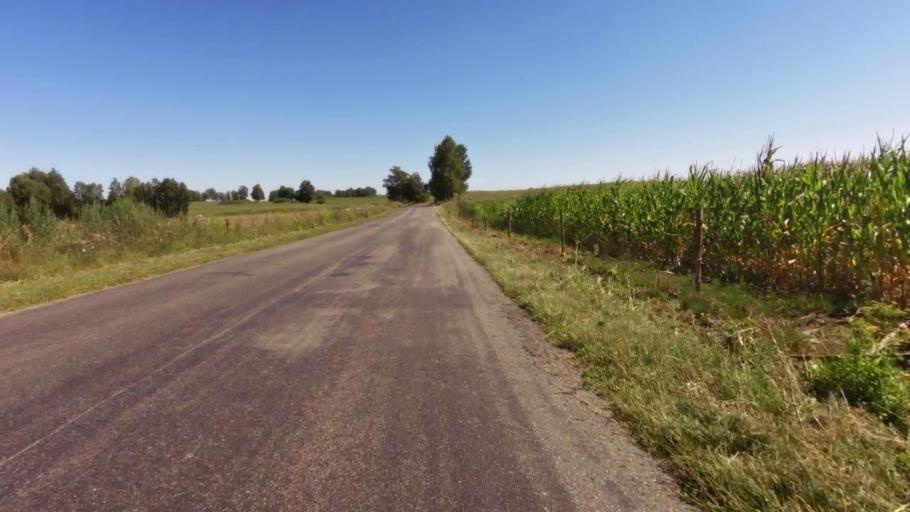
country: PL
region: West Pomeranian Voivodeship
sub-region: Powiat szczecinecki
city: Lubowo
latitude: 53.5854
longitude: 16.4108
